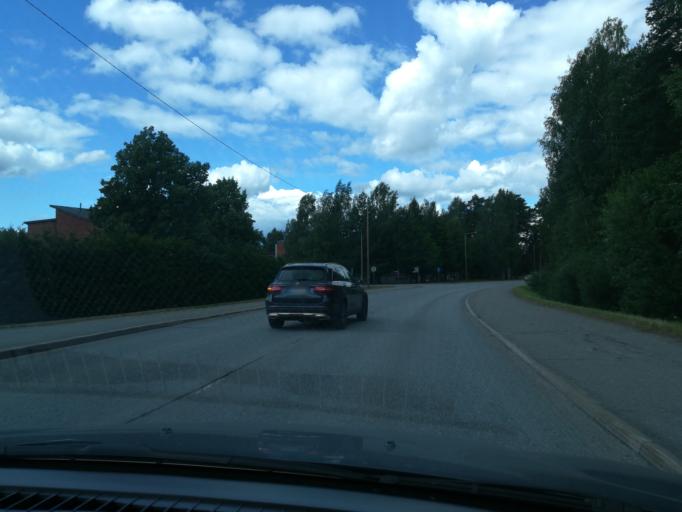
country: FI
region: Southern Savonia
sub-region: Mikkeli
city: Maentyharju
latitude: 61.4126
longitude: 26.8823
